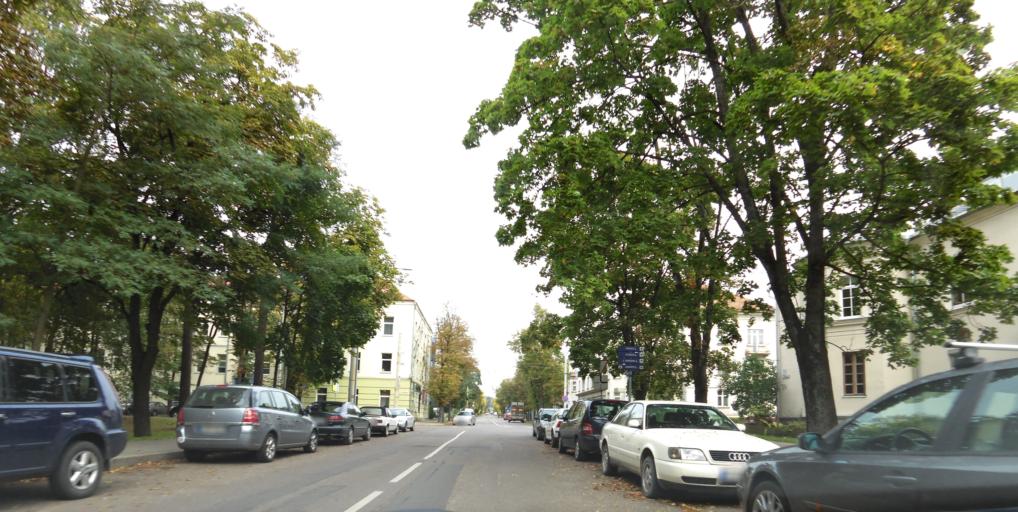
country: LT
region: Vilnius County
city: Naujamiestis
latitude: 54.6882
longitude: 25.2523
